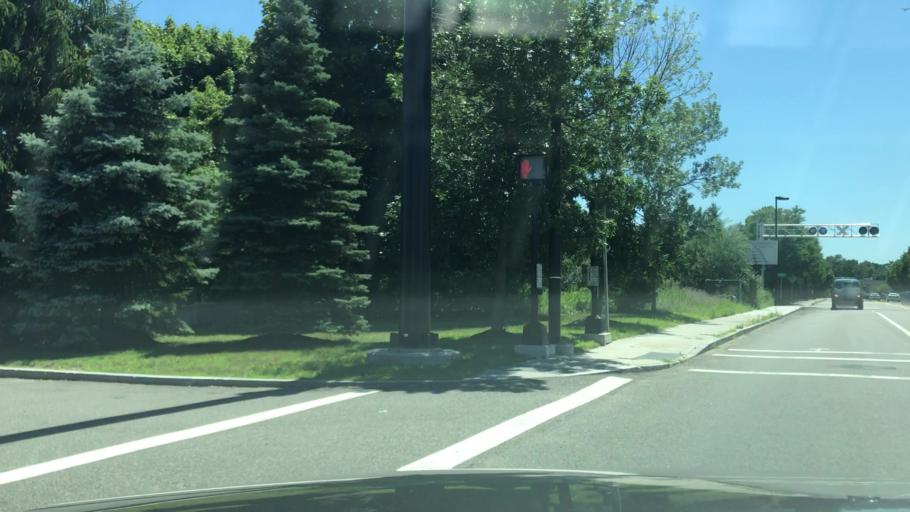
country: US
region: Massachusetts
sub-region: Norfolk County
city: Dedham
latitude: 42.2018
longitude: -71.1543
